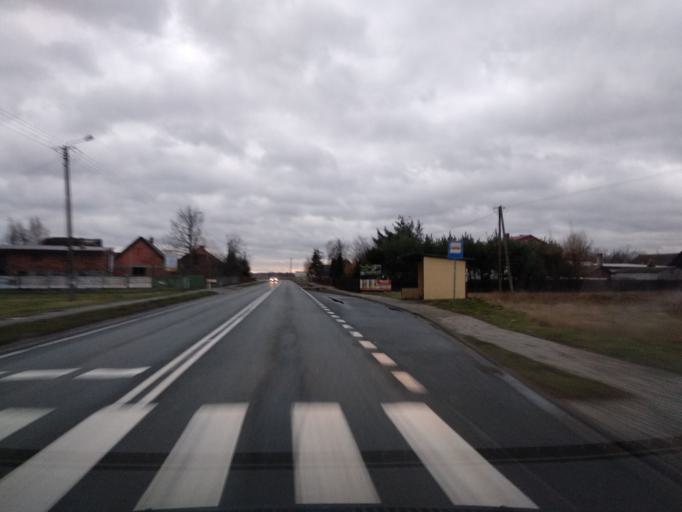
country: PL
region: Greater Poland Voivodeship
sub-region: Powiat koninski
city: Rychwal
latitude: 52.1184
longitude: 18.1684
